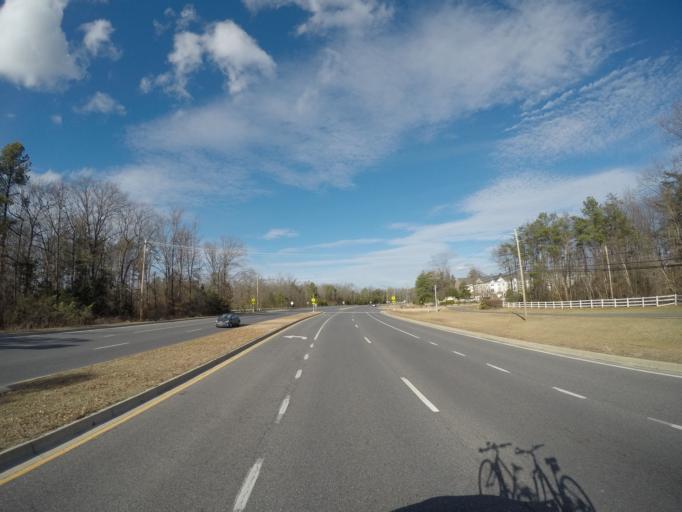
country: US
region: Maryland
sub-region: Charles County
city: Waldorf
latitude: 38.6272
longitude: -76.9682
